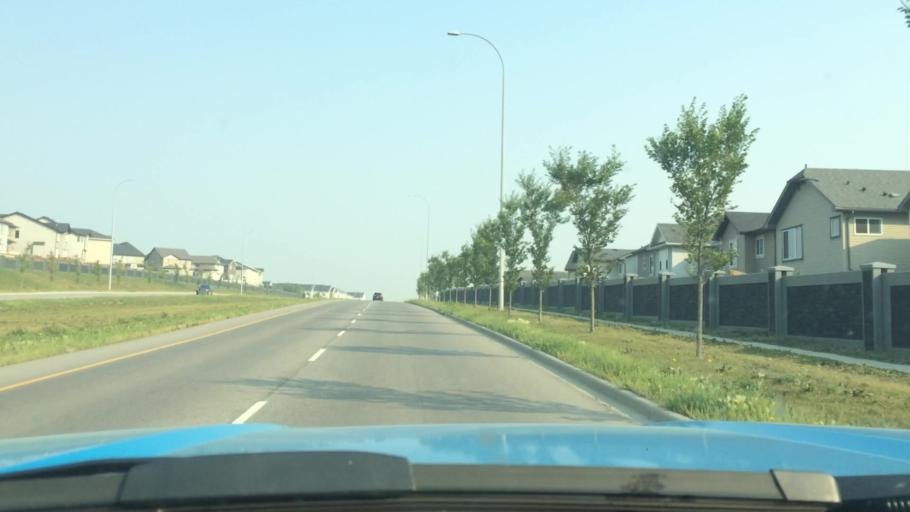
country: CA
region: Alberta
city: Calgary
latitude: 51.1769
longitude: -114.1577
